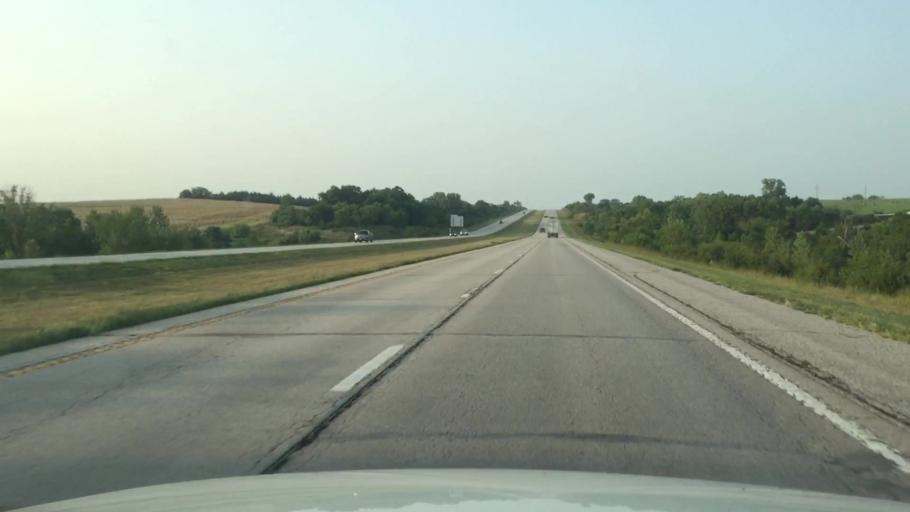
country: US
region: Iowa
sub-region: Decatur County
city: Lamoni
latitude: 40.4793
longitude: -93.9731
